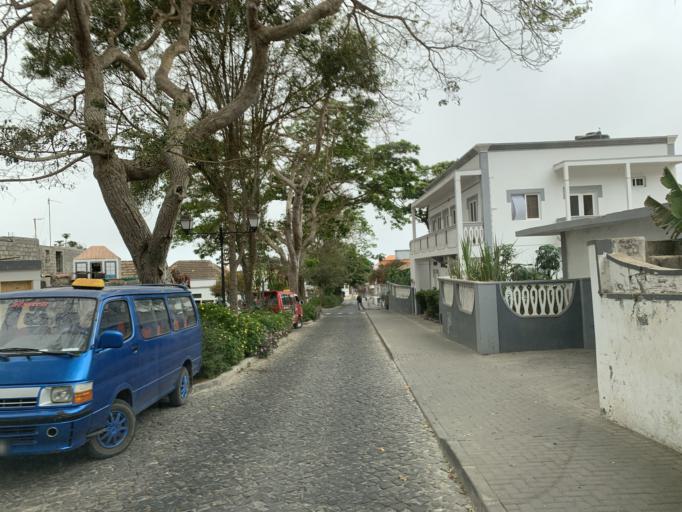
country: CV
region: Brava
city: Vila Nova Sintra
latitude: 14.8707
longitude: -24.6971
